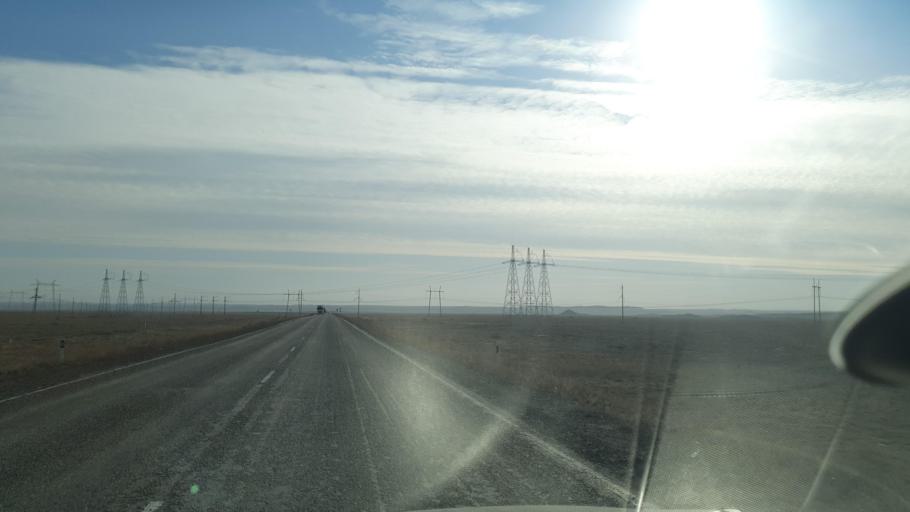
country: KZ
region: Zhambyl
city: Mynaral
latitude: 45.6034
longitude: 73.3982
